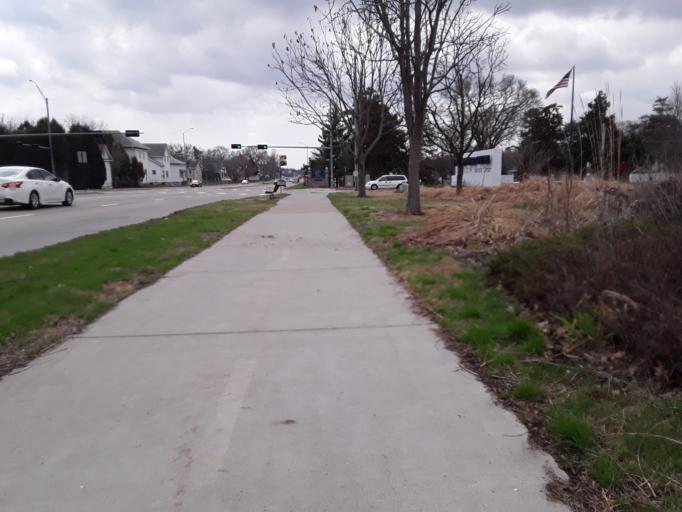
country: US
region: Nebraska
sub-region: Lancaster County
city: Lincoln
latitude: 40.8323
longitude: -96.6824
